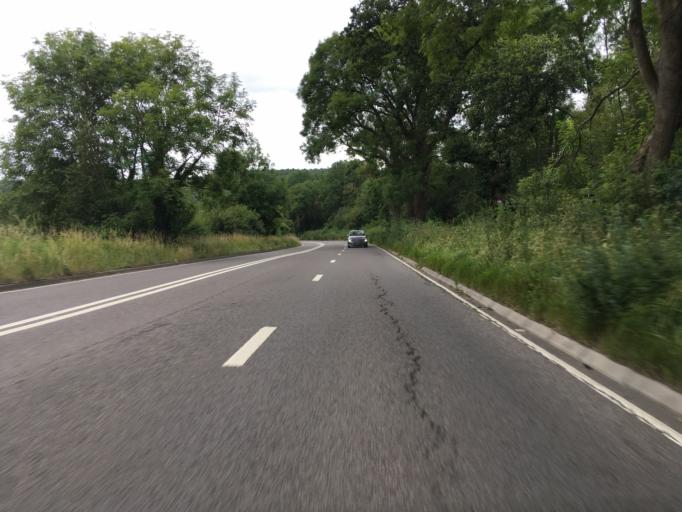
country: GB
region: England
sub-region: Gloucestershire
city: Charlton Kings
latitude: 51.8823
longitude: -1.9938
